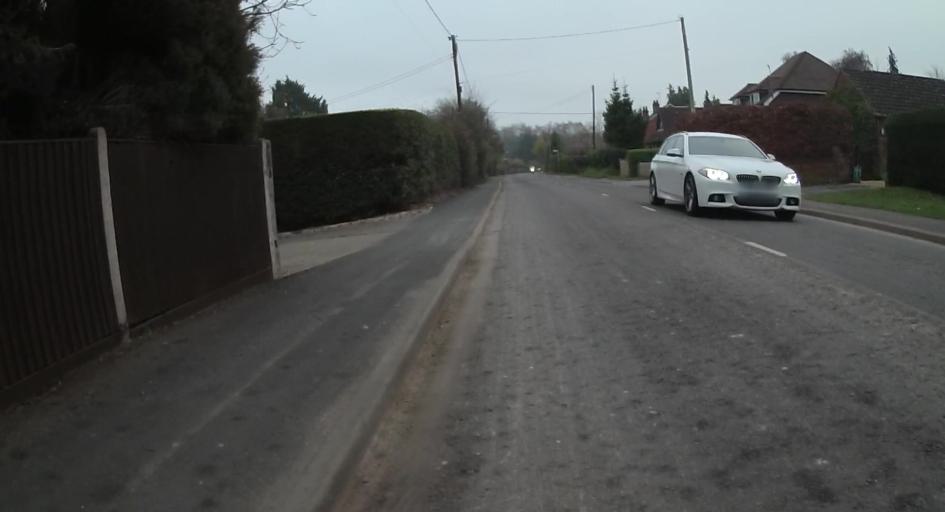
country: GB
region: England
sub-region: Hampshire
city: Kings Worthy
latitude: 51.1019
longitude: -1.3044
